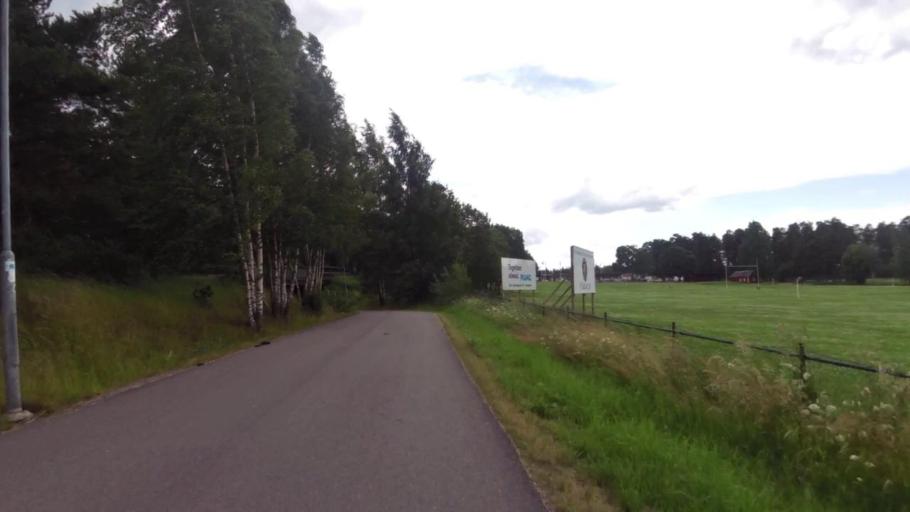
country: SE
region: OEstergoetland
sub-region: Linkopings Kommun
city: Linkoping
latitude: 58.4045
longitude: 15.5719
